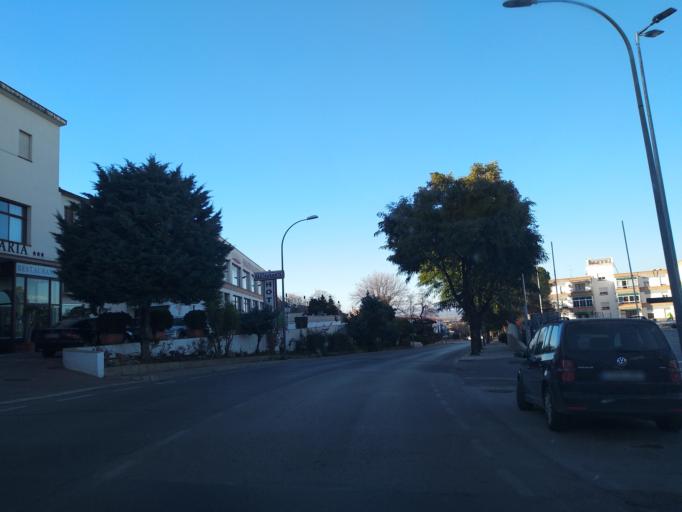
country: ES
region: Andalusia
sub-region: Provincia de Malaga
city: Antequera
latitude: 37.0236
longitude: -4.5606
